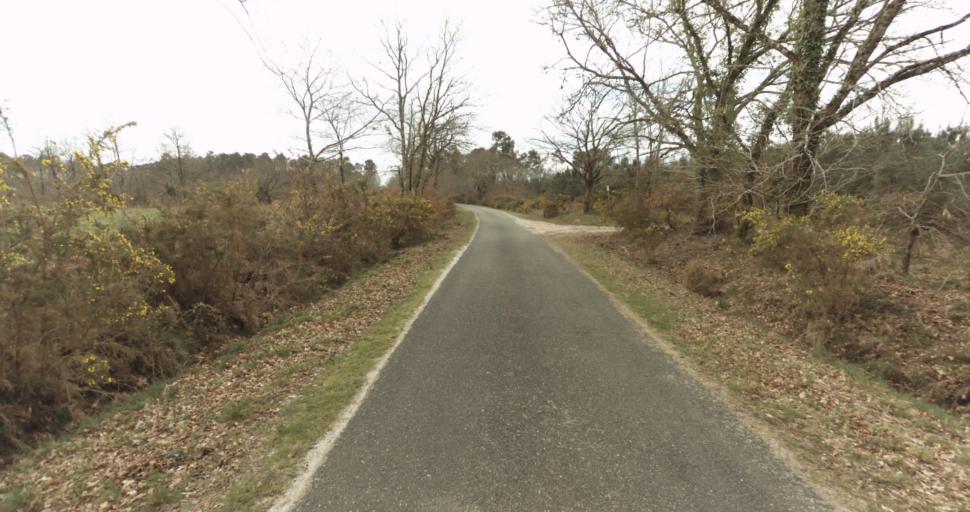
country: FR
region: Aquitaine
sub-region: Departement des Landes
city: Roquefort
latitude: 44.0866
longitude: -0.4417
